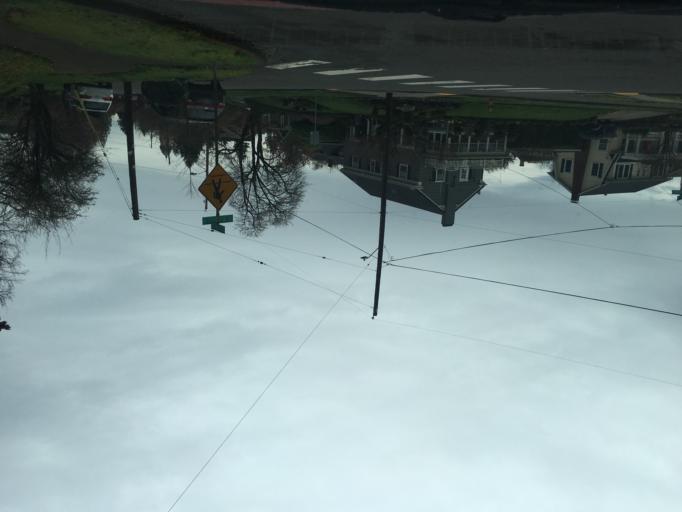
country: US
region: Oregon
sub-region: Multnomah County
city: Portland
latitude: 45.5418
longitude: -122.6110
